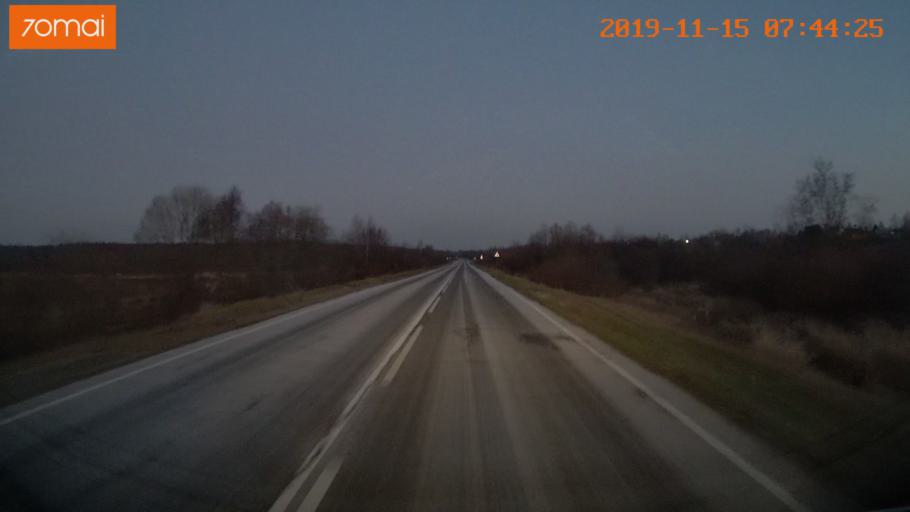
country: RU
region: Vologda
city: Sheksna
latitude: 58.8128
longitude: 38.3138
